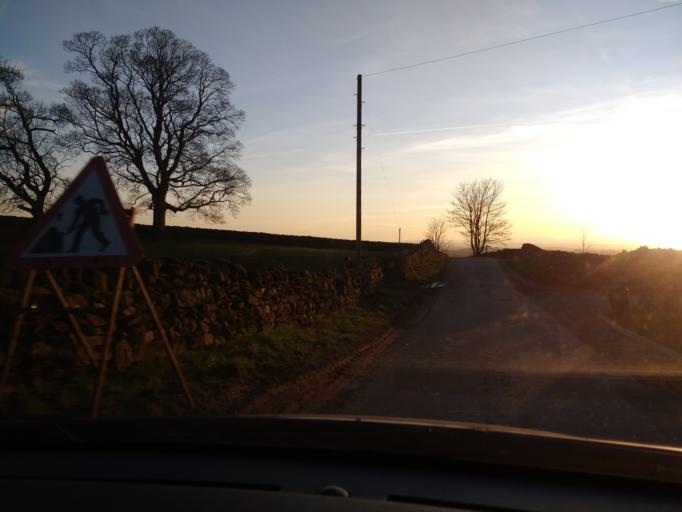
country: GB
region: England
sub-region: Cumbria
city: Appleby-in-Westmorland
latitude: 54.6122
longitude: -2.4808
